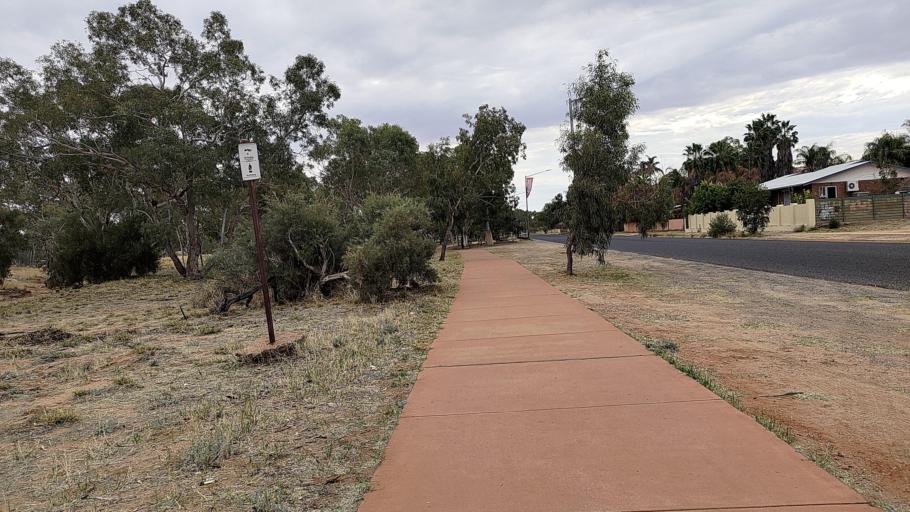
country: AU
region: Northern Territory
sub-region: Alice Springs
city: Alice Springs
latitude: -23.7103
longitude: 133.8806
